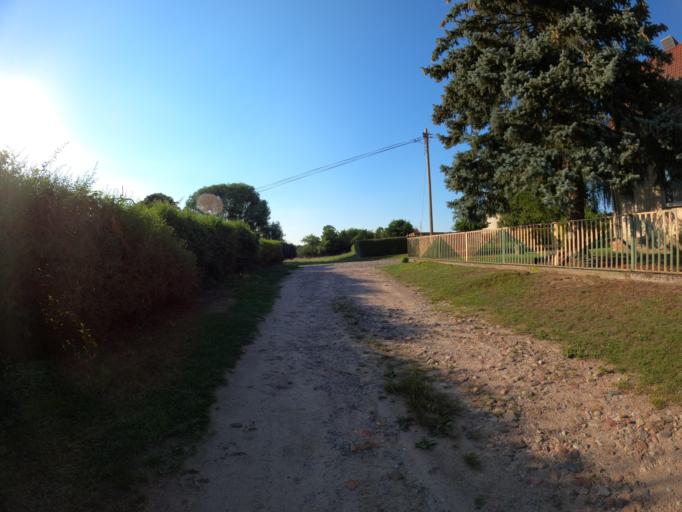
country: DE
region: Brandenburg
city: Tantow
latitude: 53.2515
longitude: 14.3634
